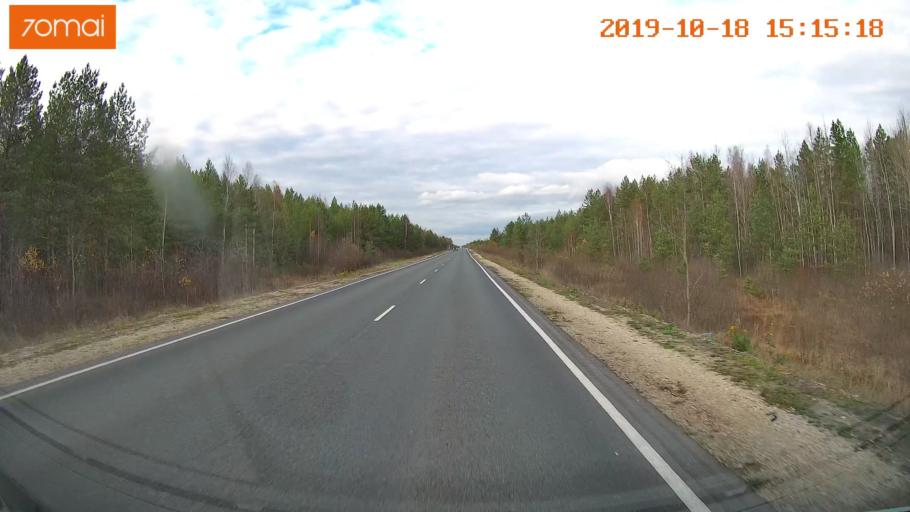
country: RU
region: Vladimir
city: Gus'-Khrustal'nyy
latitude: 55.6168
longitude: 40.7222
